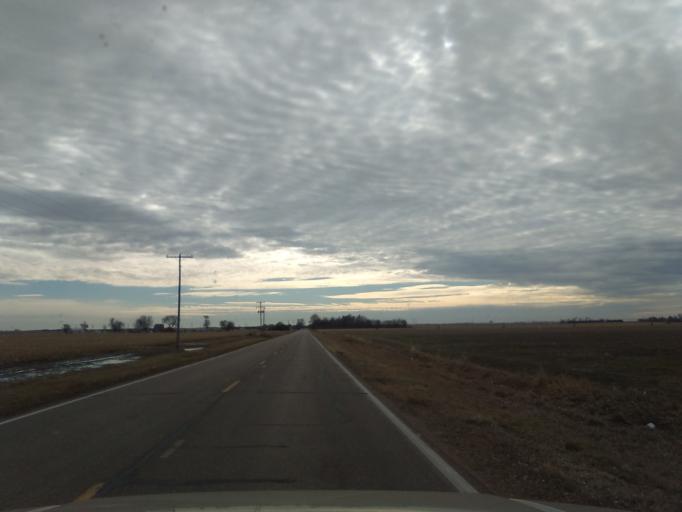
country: US
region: Nebraska
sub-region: Buffalo County
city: Gibbon
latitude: 40.6546
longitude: -98.8474
